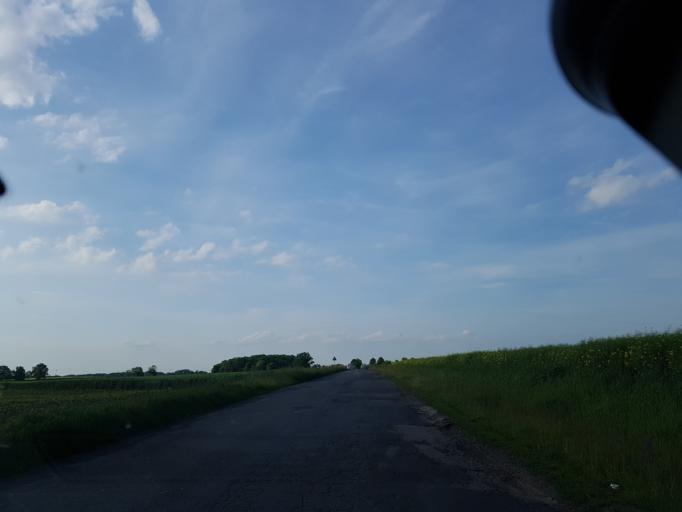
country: PL
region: Lower Silesian Voivodeship
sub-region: Powiat wroclawski
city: Zorawina
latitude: 50.9114
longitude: 17.0024
